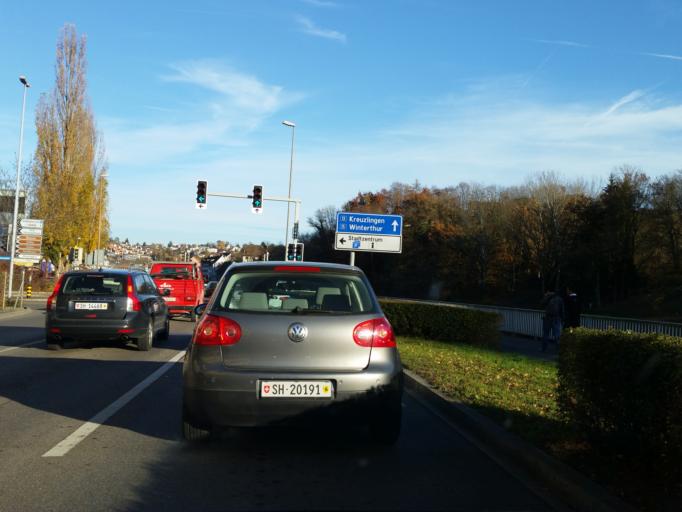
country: CH
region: Schaffhausen
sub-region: Bezirk Schaffhausen
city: Schaffhausen
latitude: 47.6935
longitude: 8.6347
